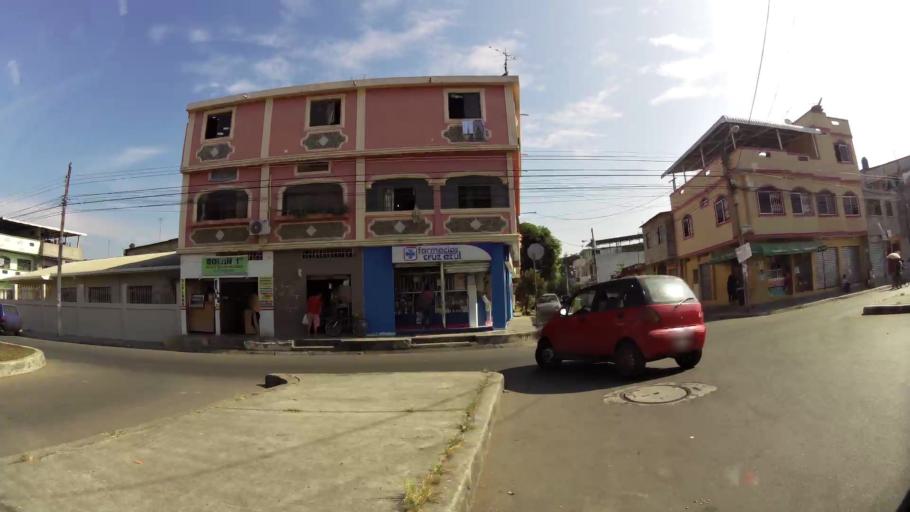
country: EC
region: Guayas
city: Eloy Alfaro
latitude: -2.0864
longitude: -79.9163
